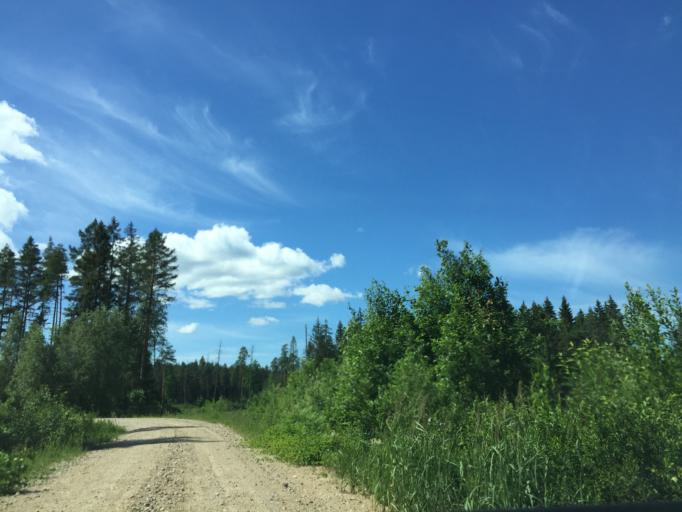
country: LV
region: Kuldigas Rajons
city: Kuldiga
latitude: 57.1104
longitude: 21.8635
